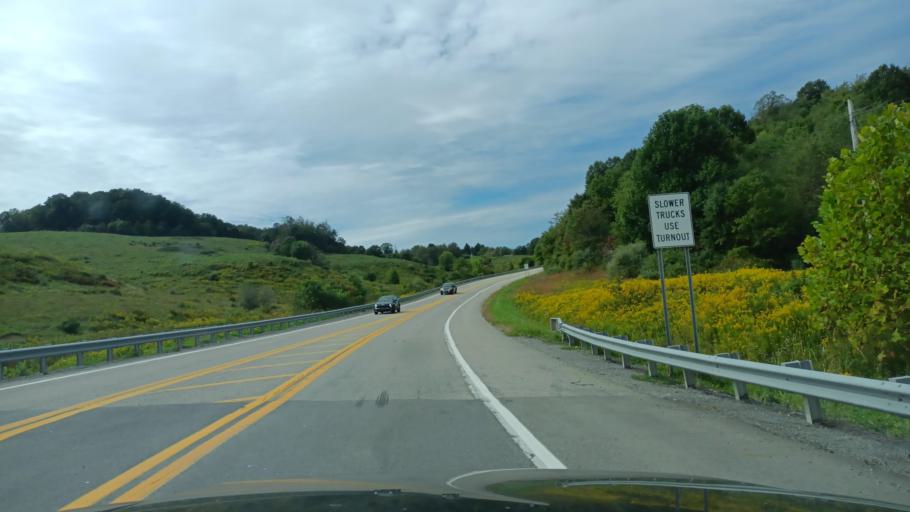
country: US
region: West Virginia
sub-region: Taylor County
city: Grafton
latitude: 39.3142
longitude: -80.1336
